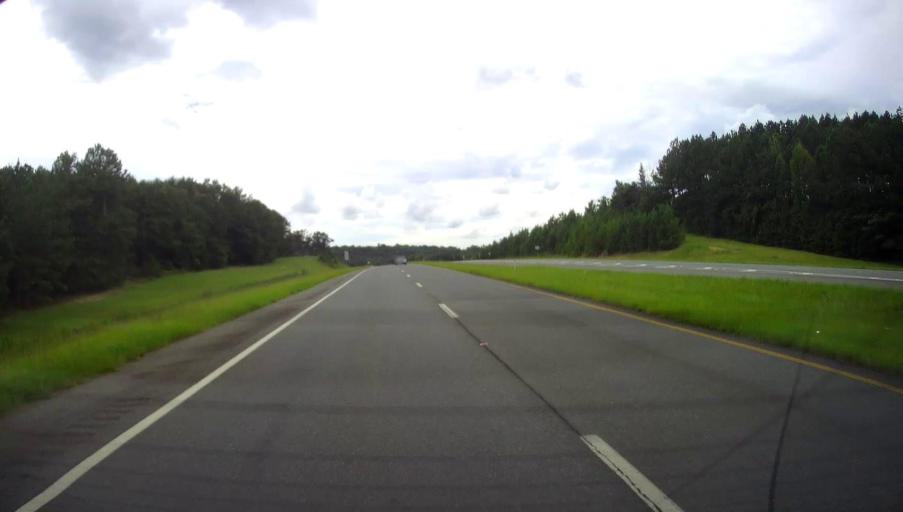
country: US
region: Georgia
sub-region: Schley County
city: Ellaville
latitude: 32.2708
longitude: -84.3004
